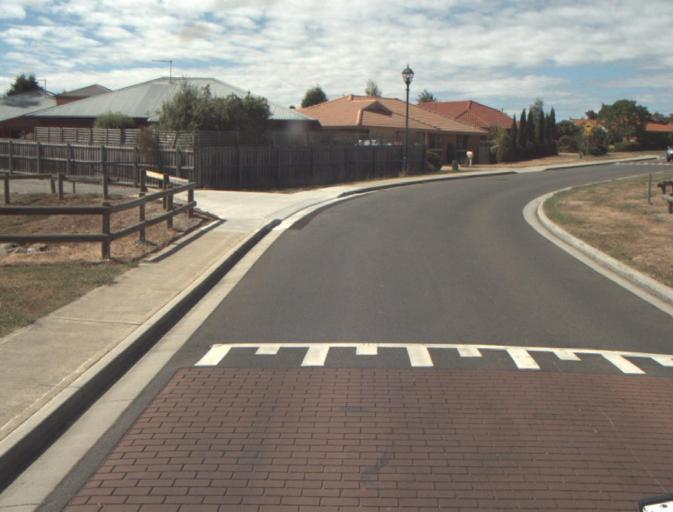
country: AU
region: Tasmania
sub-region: Launceston
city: Summerhill
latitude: -41.4729
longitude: 147.1163
